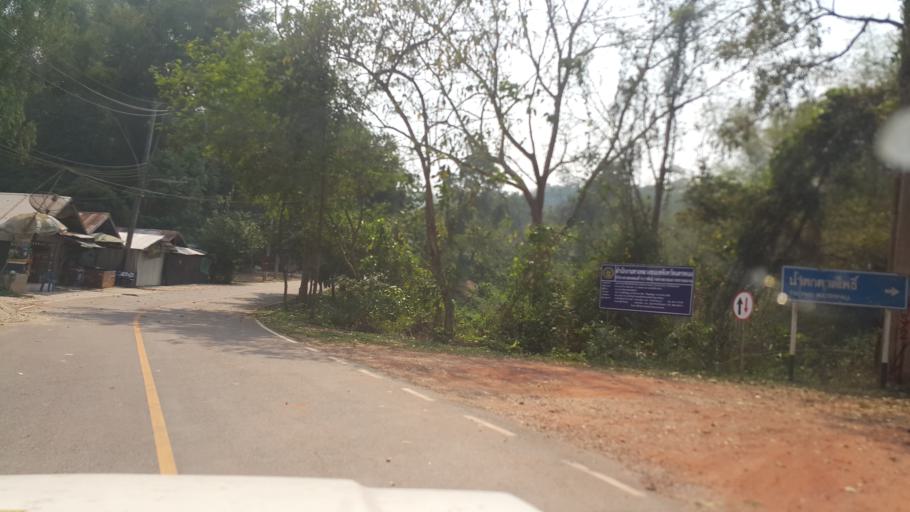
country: TH
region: Nakhon Phanom
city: Ban Phaeng
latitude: 17.9540
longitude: 104.1605
